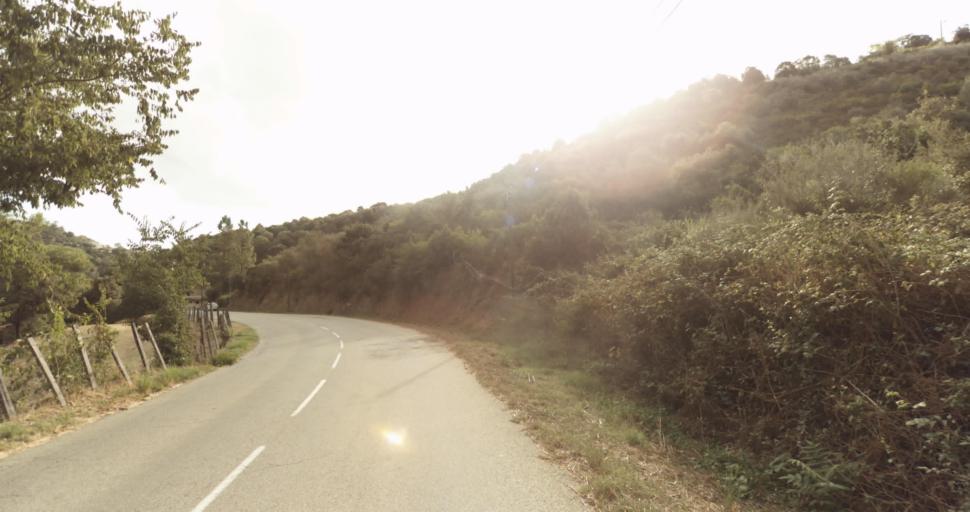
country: FR
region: Corsica
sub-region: Departement de la Corse-du-Sud
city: Ajaccio
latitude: 41.9290
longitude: 8.7055
